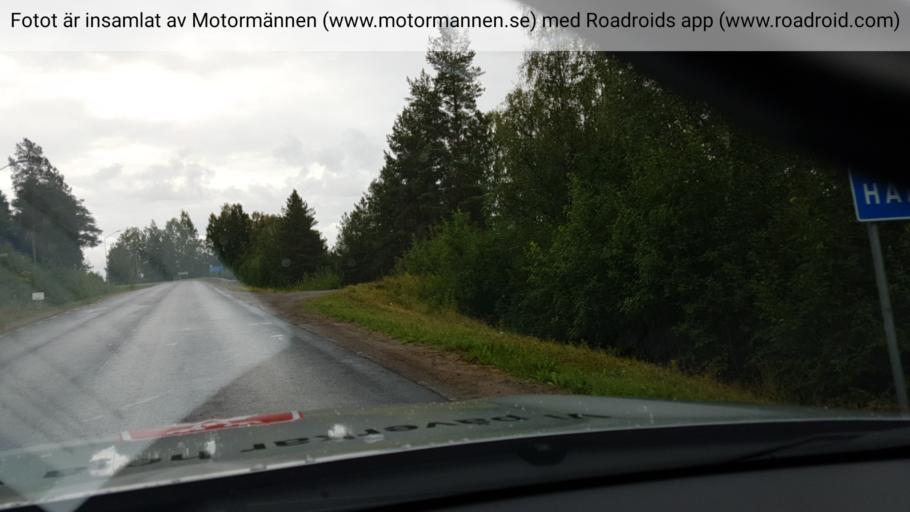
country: SE
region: Norrbotten
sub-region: Alvsbyns Kommun
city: AElvsbyn
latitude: 66.0900
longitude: 20.9464
